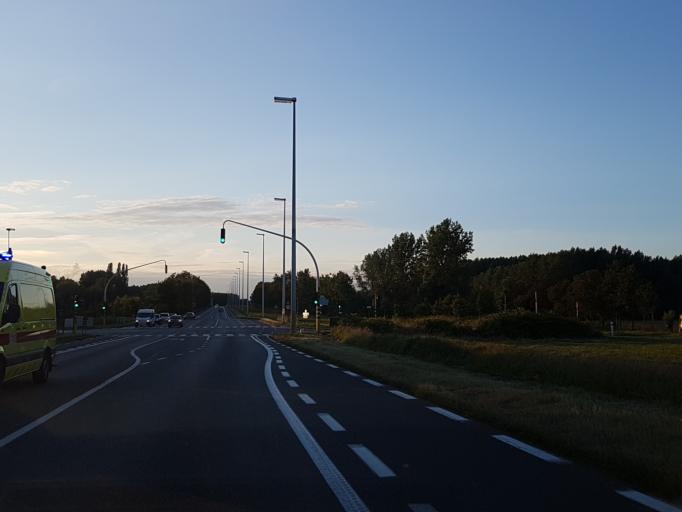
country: BE
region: Flanders
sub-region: Provincie Oost-Vlaanderen
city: Hamme
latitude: 51.1007
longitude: 4.1474
